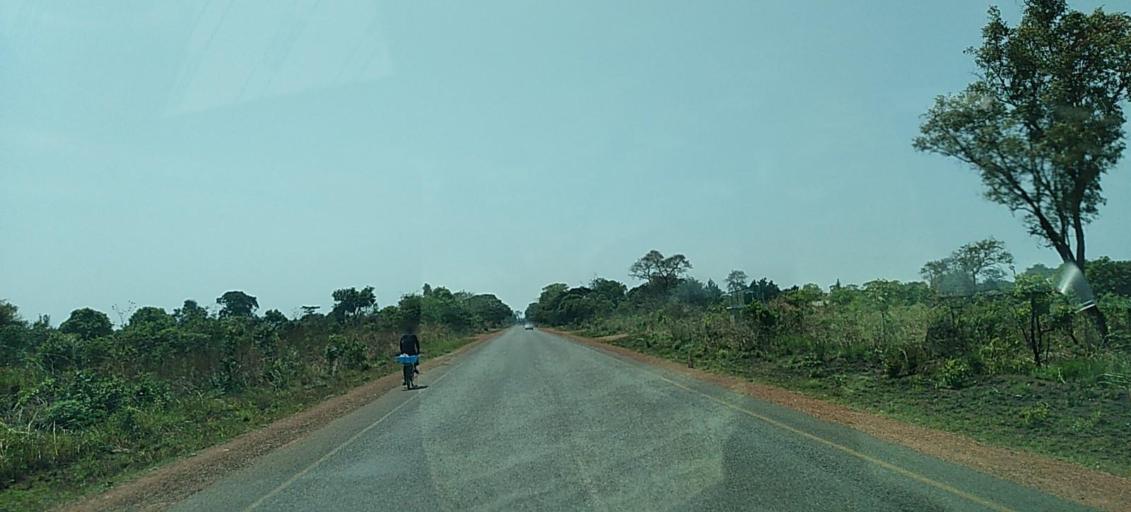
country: ZM
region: North-Western
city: Solwezi
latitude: -12.3192
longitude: 25.8683
